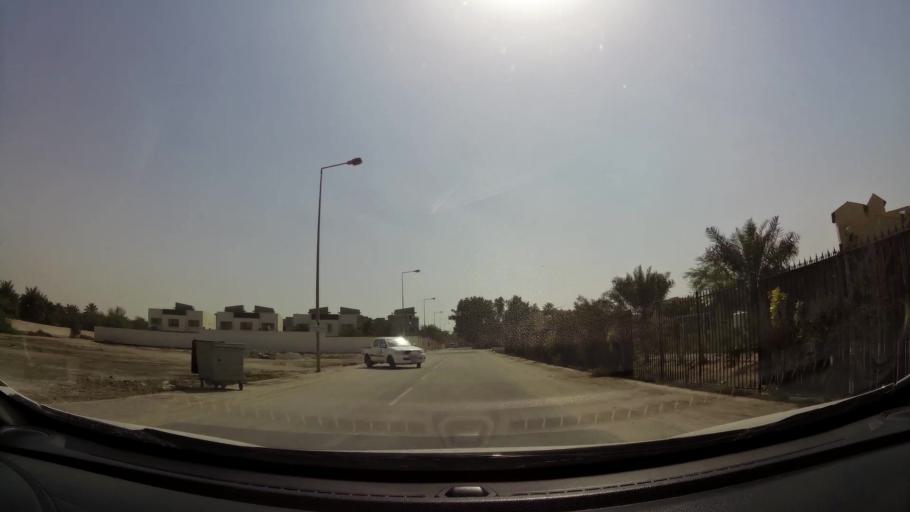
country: BH
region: Northern
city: Madinat `Isa
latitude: 26.1928
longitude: 50.4609
